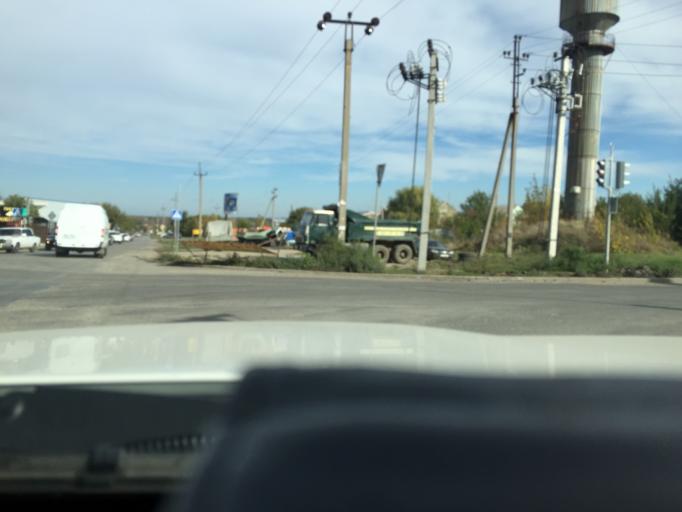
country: RU
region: Rostov
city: Imeni Chkalova
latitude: 47.2981
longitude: 39.8036
